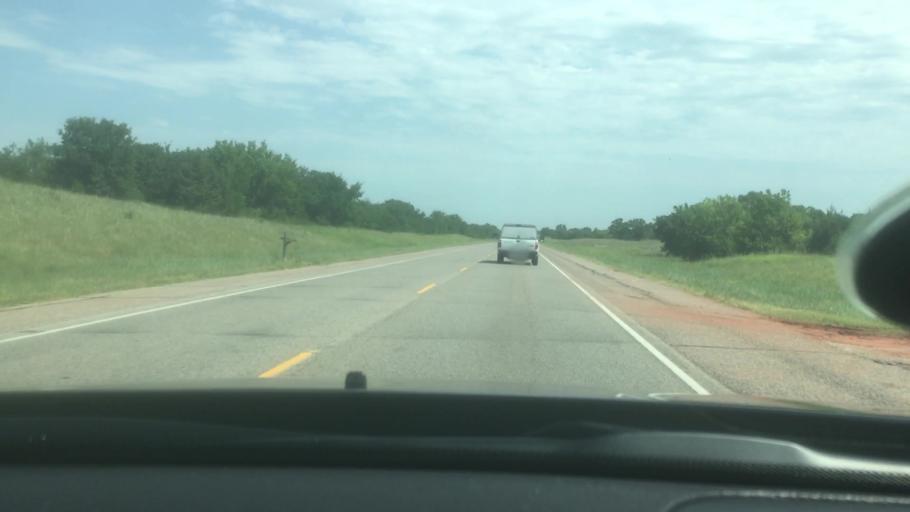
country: US
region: Oklahoma
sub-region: Seminole County
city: Maud
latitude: 35.0328
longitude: -96.9314
